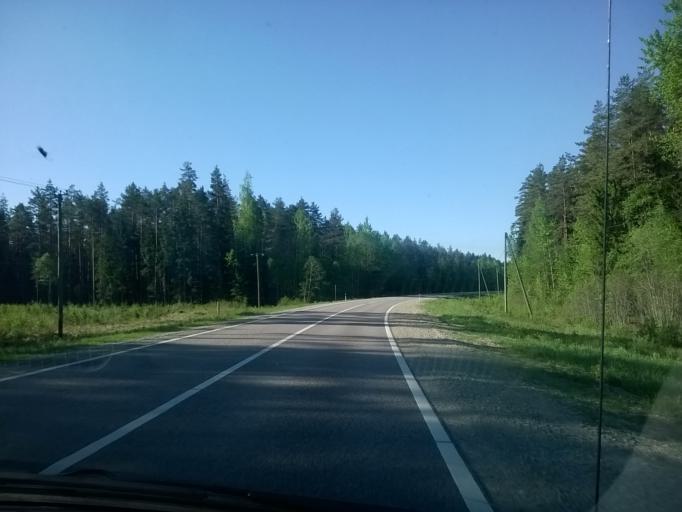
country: LV
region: Valkas Rajons
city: Valka
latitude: 57.6901
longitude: 25.9002
